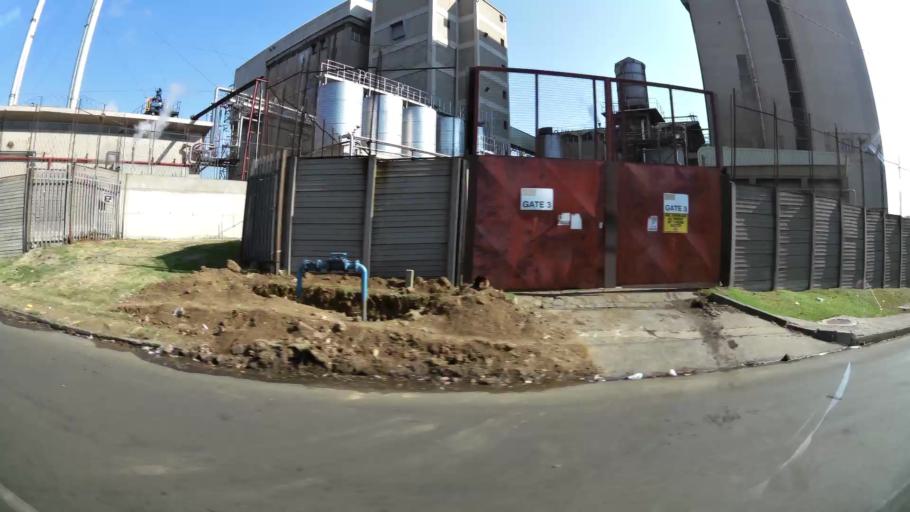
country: ZA
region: Gauteng
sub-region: City of Johannesburg Metropolitan Municipality
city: Modderfontein
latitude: -26.1351
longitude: 28.2155
